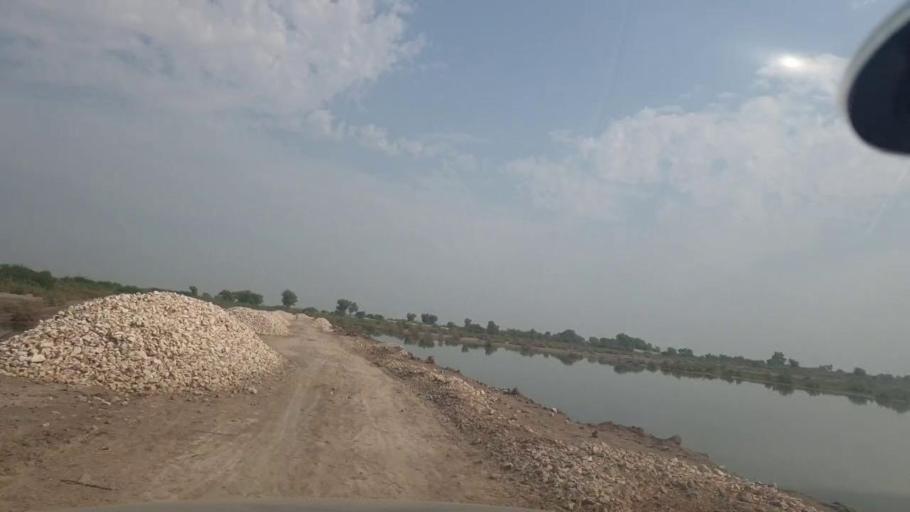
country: PK
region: Balochistan
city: Mehrabpur
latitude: 28.1136
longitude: 68.0905
